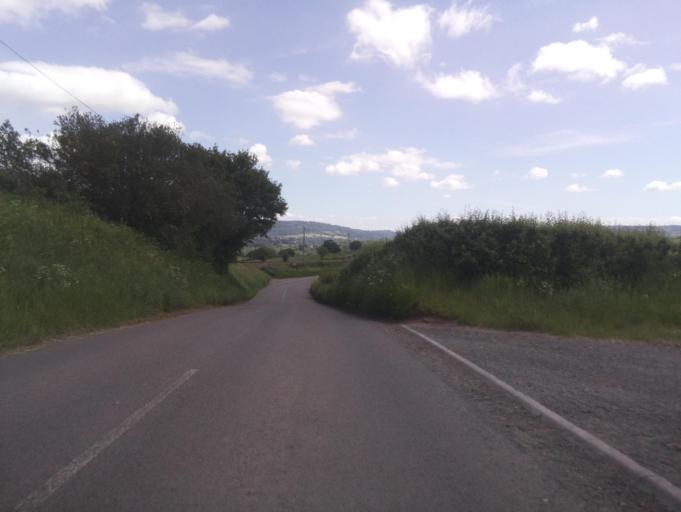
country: GB
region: England
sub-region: Herefordshire
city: Llanrothal
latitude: 51.8390
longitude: -2.7680
